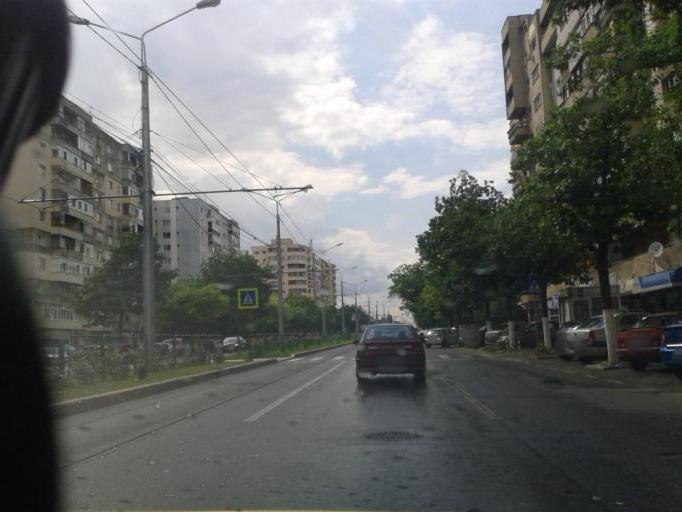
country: RO
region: Prahova
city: Ploiesti
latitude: 44.9504
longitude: 26.0033
